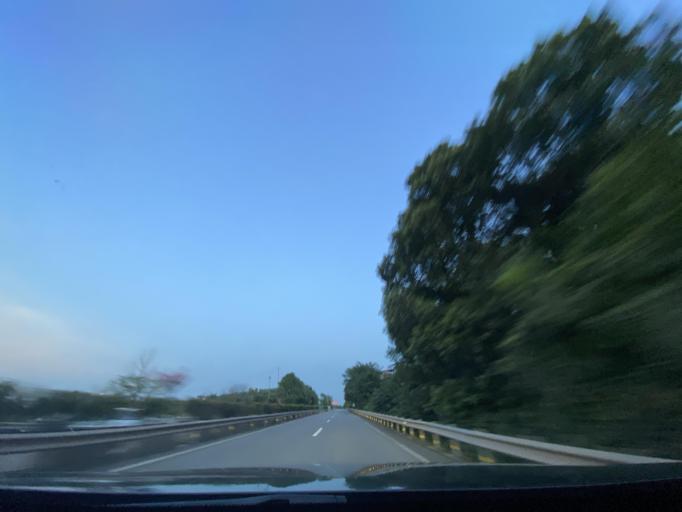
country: CN
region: Sichuan
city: Longquan
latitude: 30.4964
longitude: 104.3848
